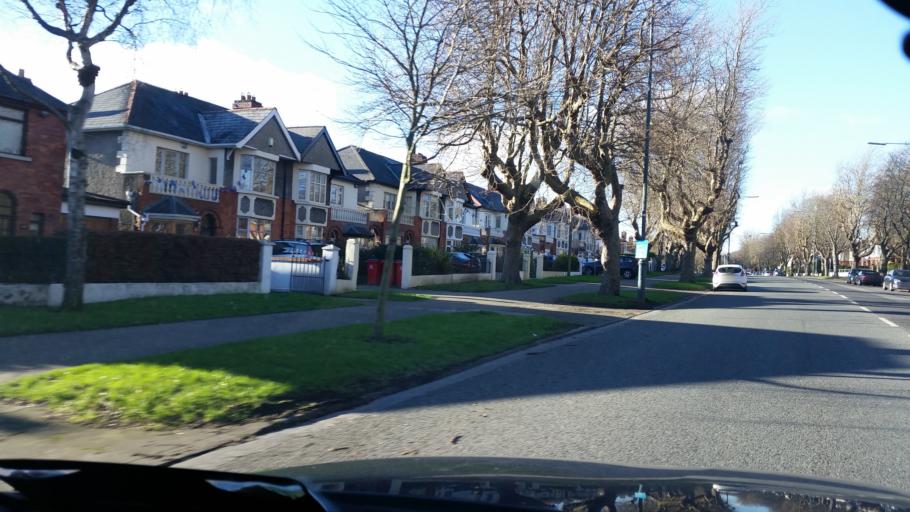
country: IE
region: Leinster
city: Marino
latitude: 53.3726
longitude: -6.2390
